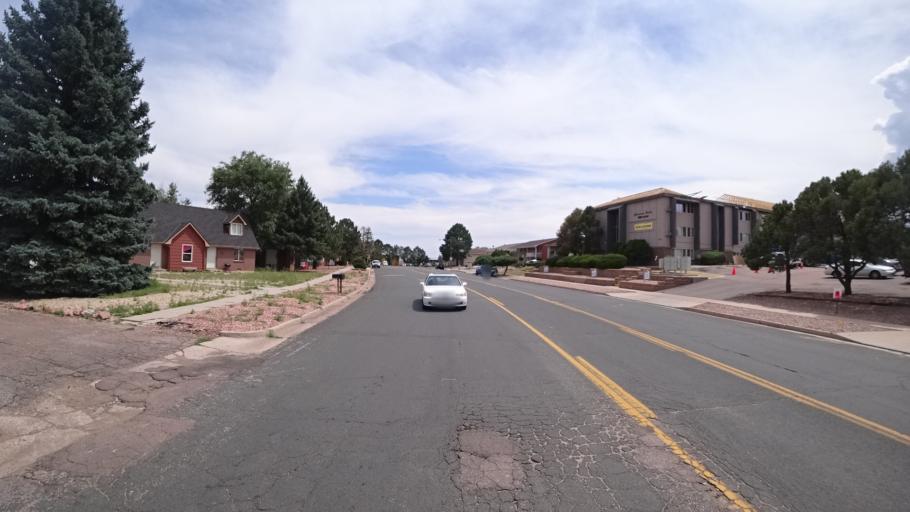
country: US
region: Colorado
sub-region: El Paso County
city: Colorado Springs
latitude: 38.8933
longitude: -104.8355
